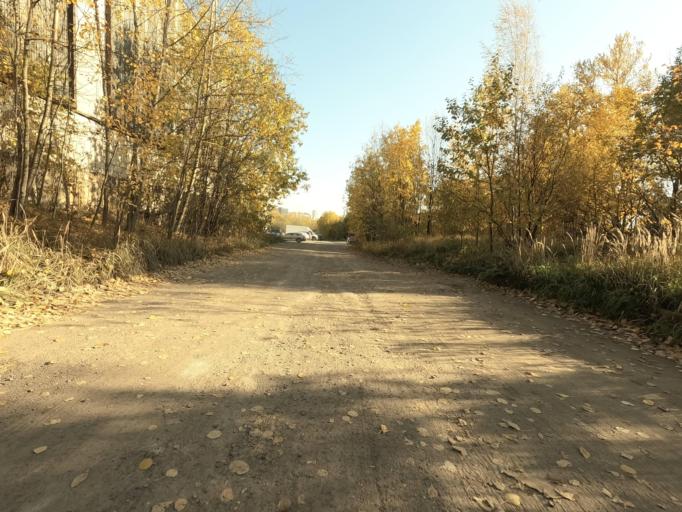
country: RU
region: Leningrad
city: Rybatskoye
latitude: 59.8413
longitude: 30.4763
